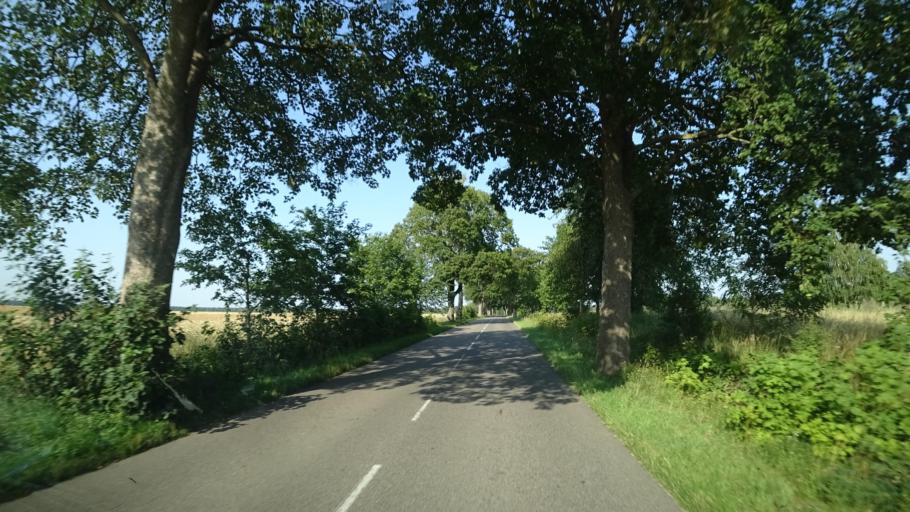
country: PL
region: Pomeranian Voivodeship
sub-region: Powiat czluchowski
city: Rzeczenica
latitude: 53.7589
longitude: 17.1276
